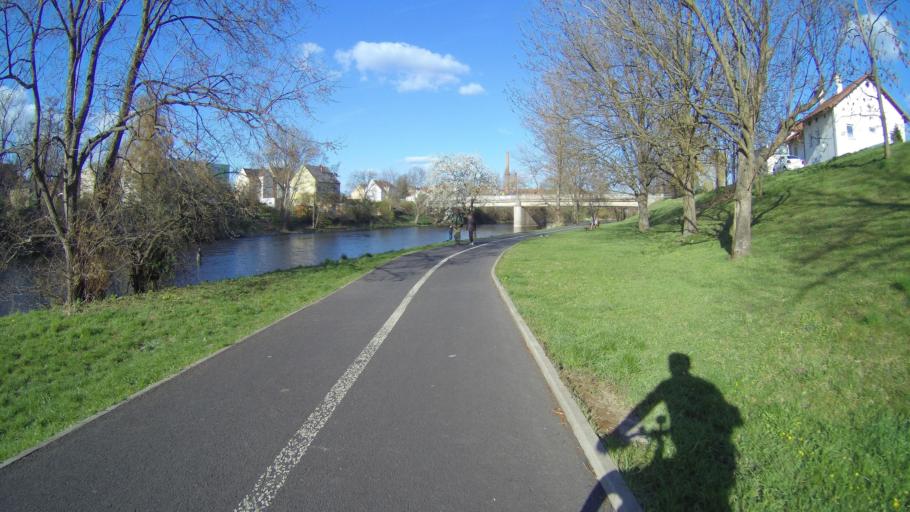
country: CZ
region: Ustecky
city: Zatec
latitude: 50.3352
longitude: 13.5411
